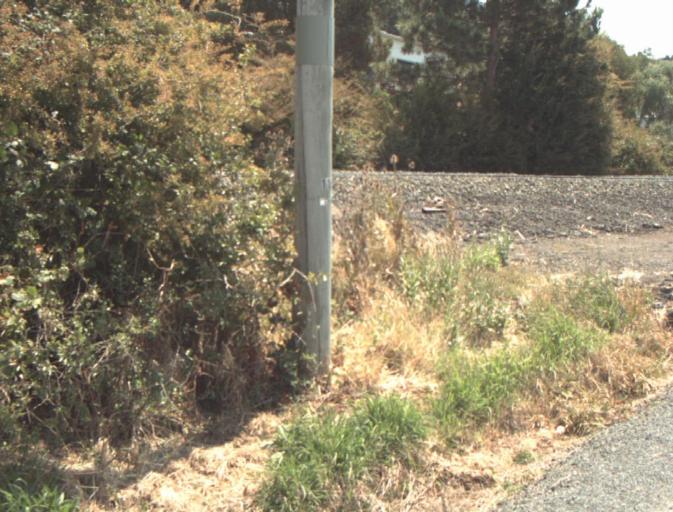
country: AU
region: Tasmania
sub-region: Launceston
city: Newstead
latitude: -41.4668
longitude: 147.1859
